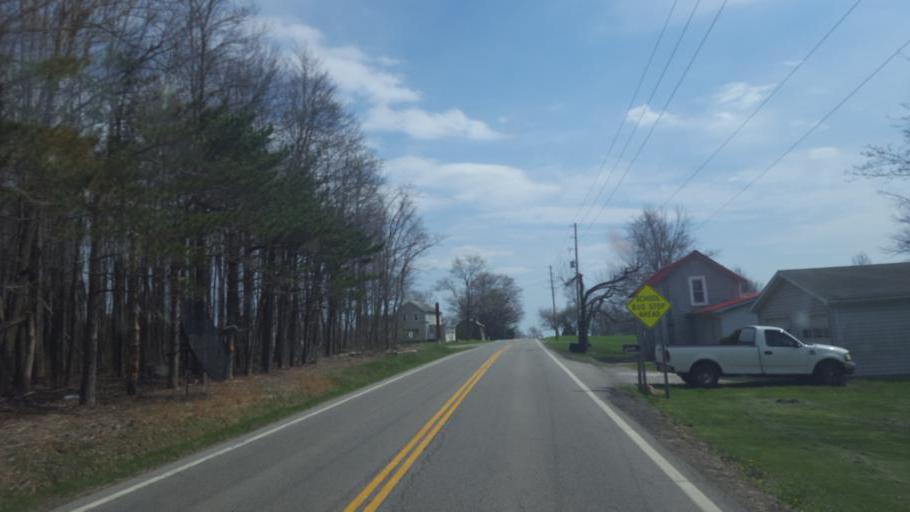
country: US
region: Ohio
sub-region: Sandusky County
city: Bellville
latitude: 40.5657
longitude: -82.5657
